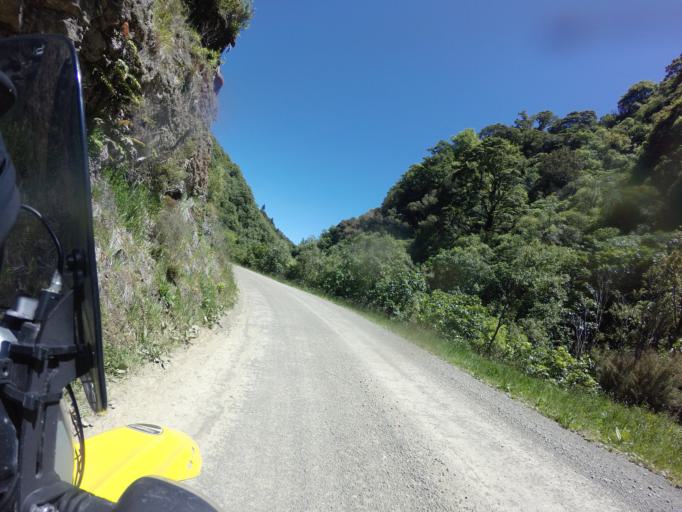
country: NZ
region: Bay of Plenty
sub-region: Opotiki District
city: Opotiki
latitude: -38.4126
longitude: 177.3946
